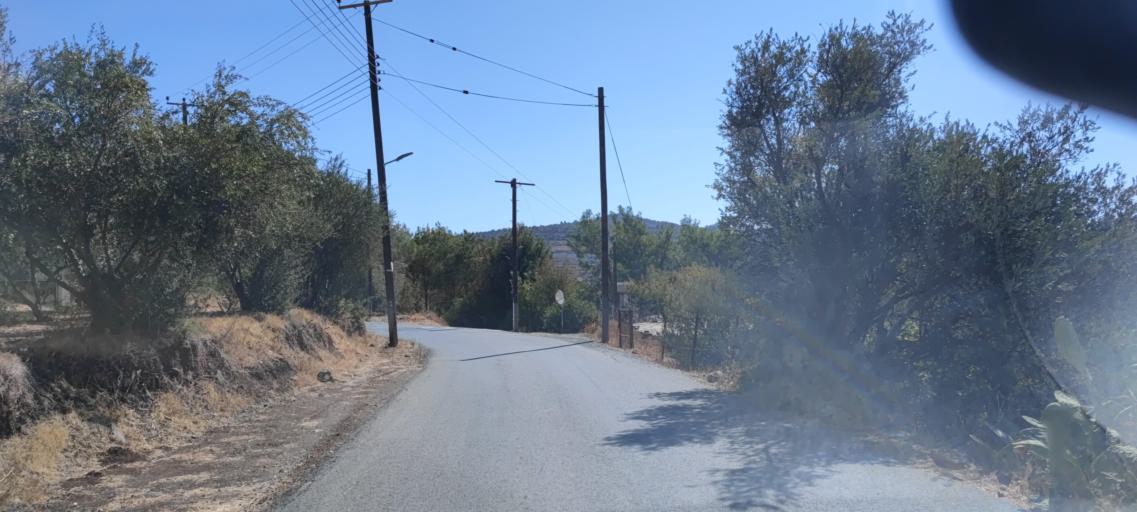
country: CY
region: Limassol
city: Mouttagiaka
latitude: 34.7585
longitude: 33.1080
